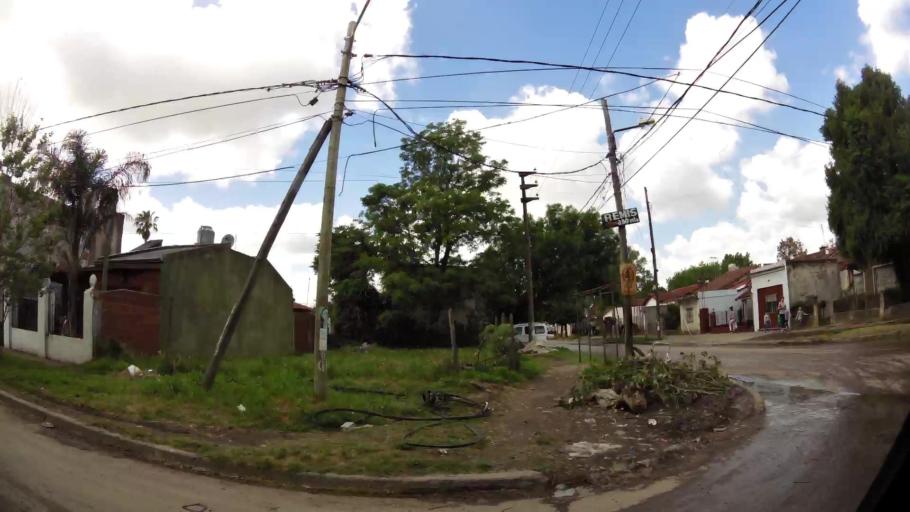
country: AR
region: Buenos Aires
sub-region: Partido de Quilmes
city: Quilmes
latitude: -34.8288
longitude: -58.2234
